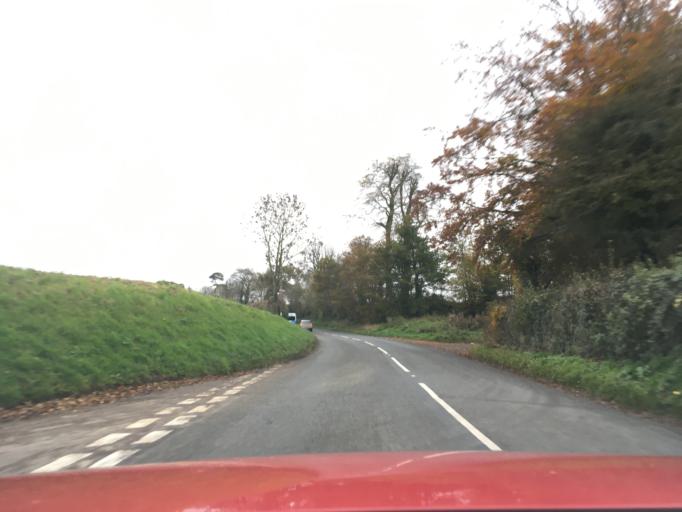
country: GB
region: England
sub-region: Dorset
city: Sherborne
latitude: 50.9642
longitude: -2.5483
